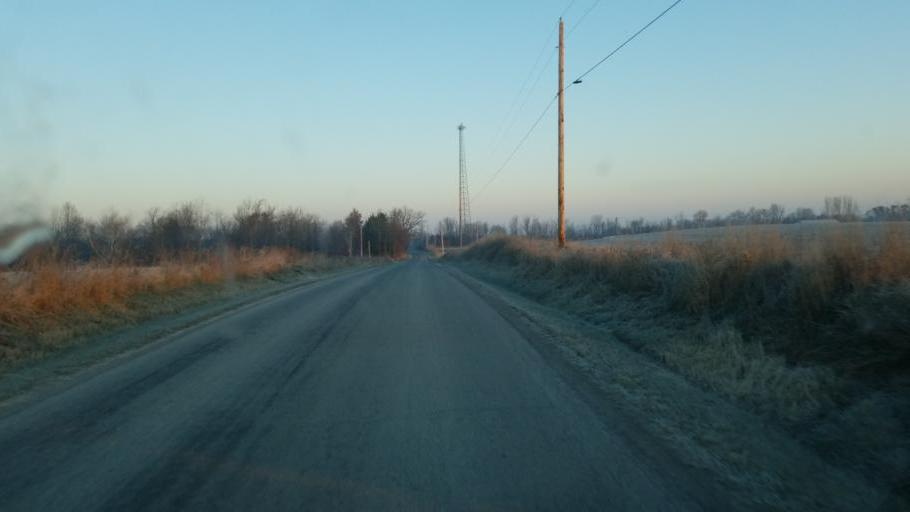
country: US
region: Ohio
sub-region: Wayne County
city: West Salem
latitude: 40.9838
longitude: -82.0544
